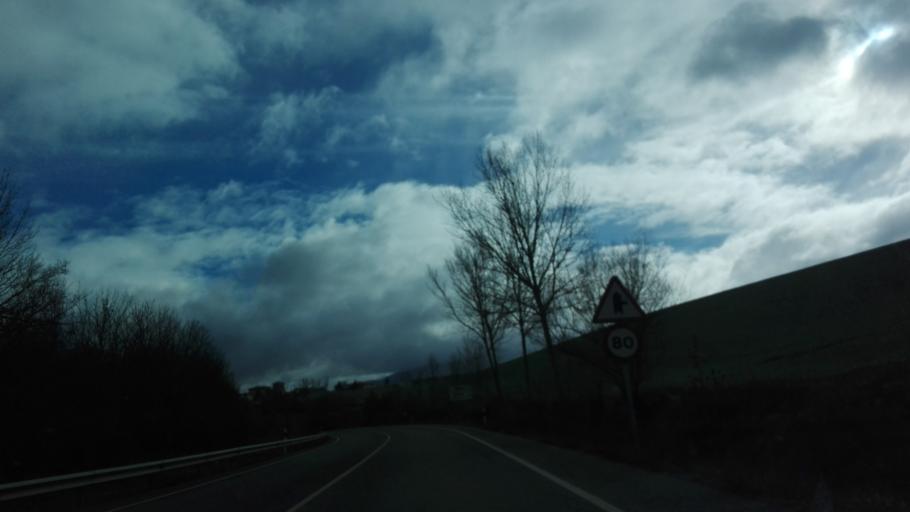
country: ES
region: Navarre
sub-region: Provincia de Navarra
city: Lizoain
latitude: 42.7837
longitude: -1.4649
